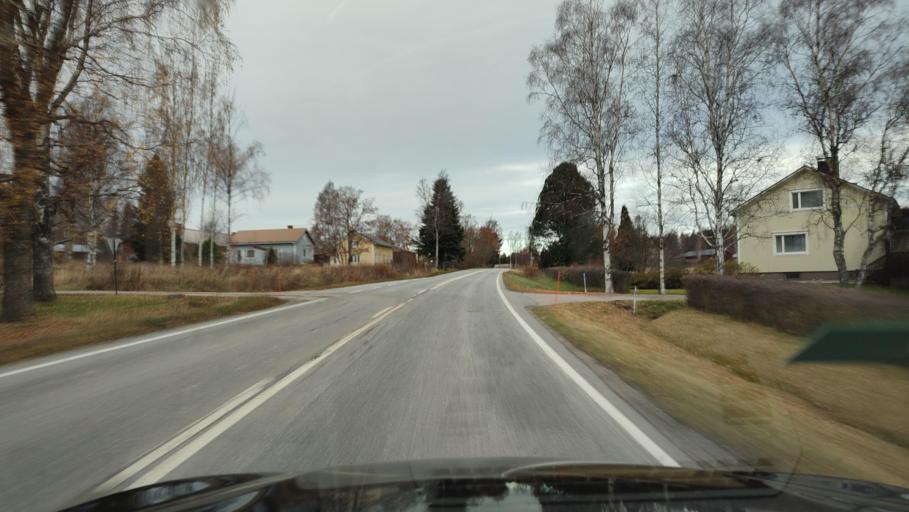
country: FI
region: Ostrobothnia
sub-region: Sydosterbotten
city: Naerpes
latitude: 62.4065
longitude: 21.3499
